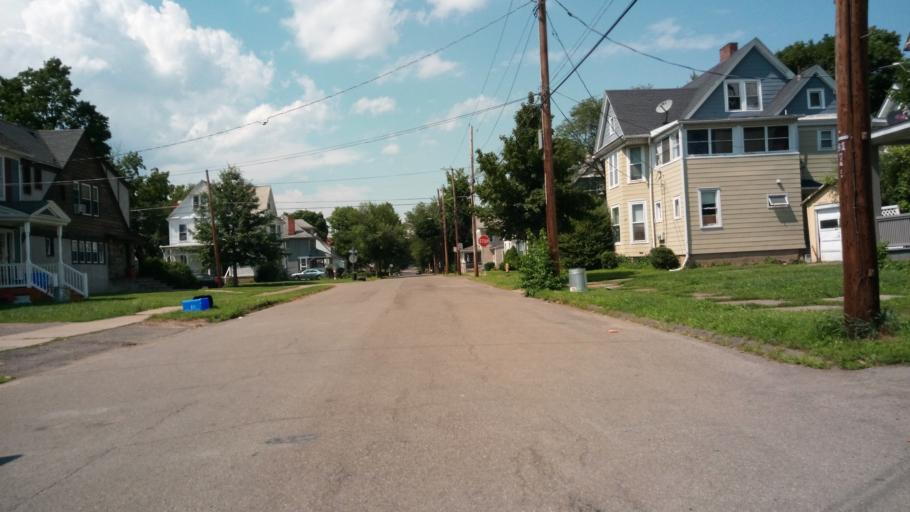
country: US
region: New York
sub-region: Chemung County
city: Elmira
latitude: 42.0851
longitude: -76.8191
